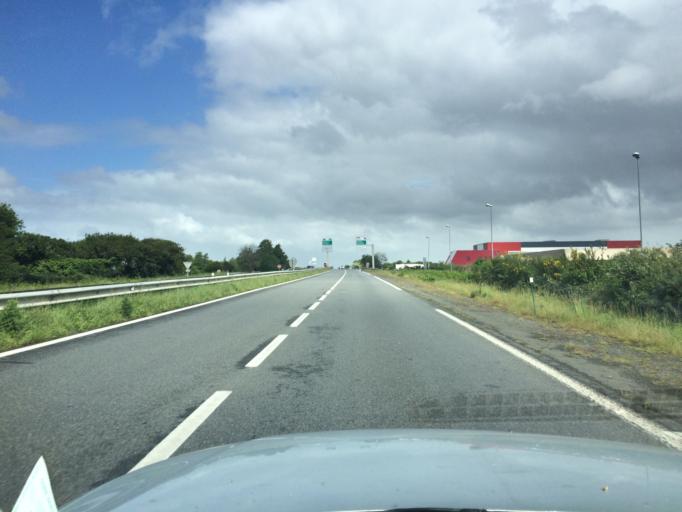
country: FR
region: Brittany
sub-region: Departement du Finistere
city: Gouesnou
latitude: 48.4330
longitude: -4.4496
